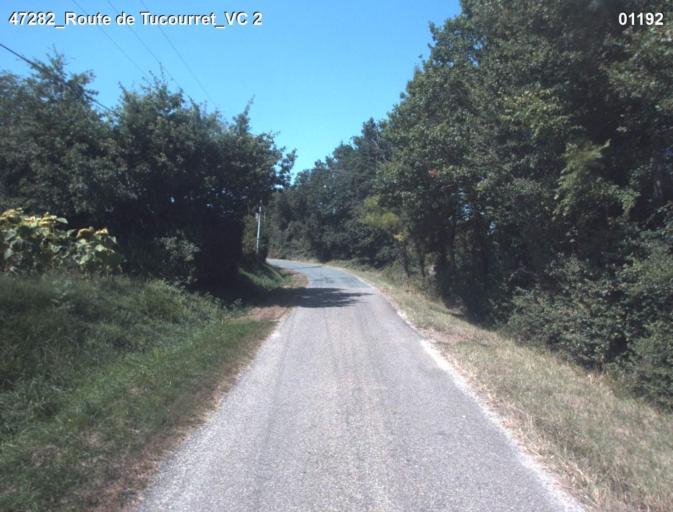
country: FR
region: Aquitaine
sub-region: Departement du Lot-et-Garonne
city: Laplume
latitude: 44.1024
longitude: 0.4851
